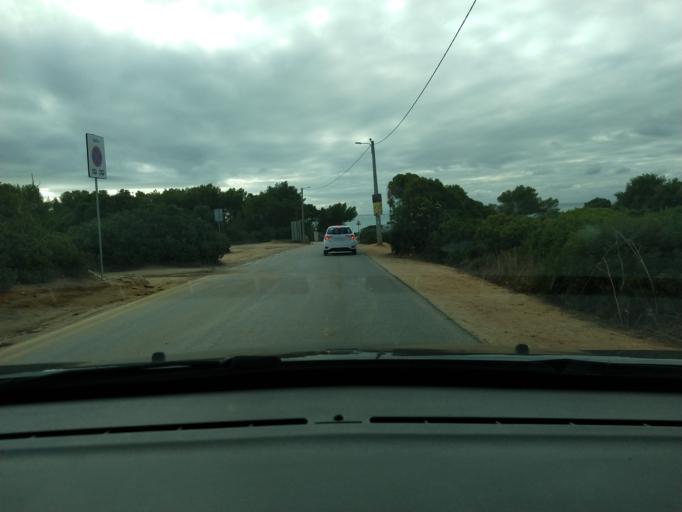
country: PT
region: Faro
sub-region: Lagoa
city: Carvoeiro
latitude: 37.0914
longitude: -8.4135
